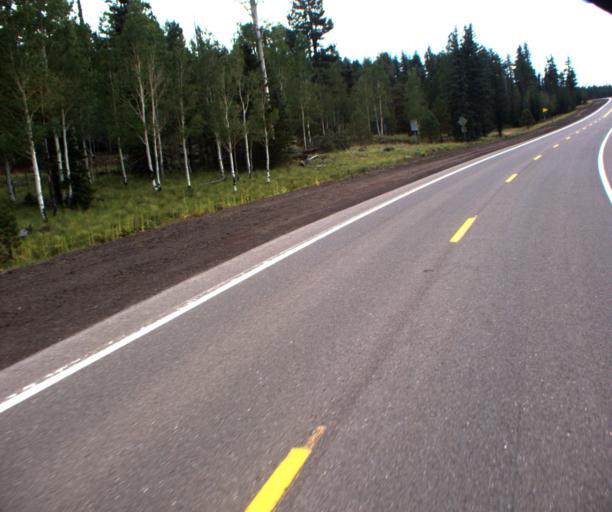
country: US
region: Arizona
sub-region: Apache County
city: Eagar
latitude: 34.0040
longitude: -109.5599
